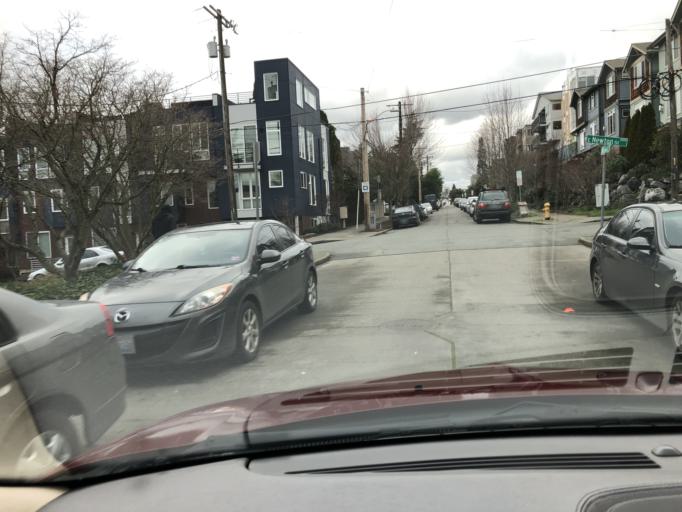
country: US
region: Washington
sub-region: King County
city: Seattle
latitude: 47.6366
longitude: -122.3270
